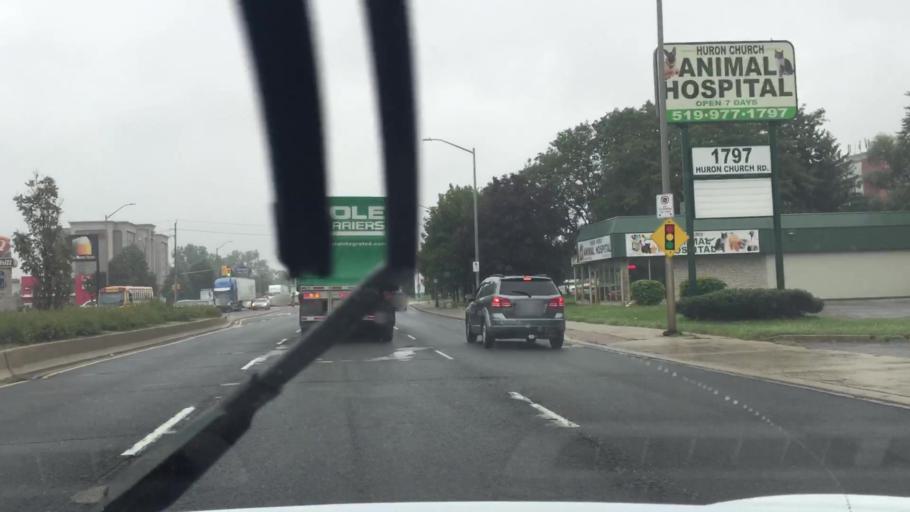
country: CA
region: Ontario
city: Windsor
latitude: 42.2837
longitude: -83.0557
